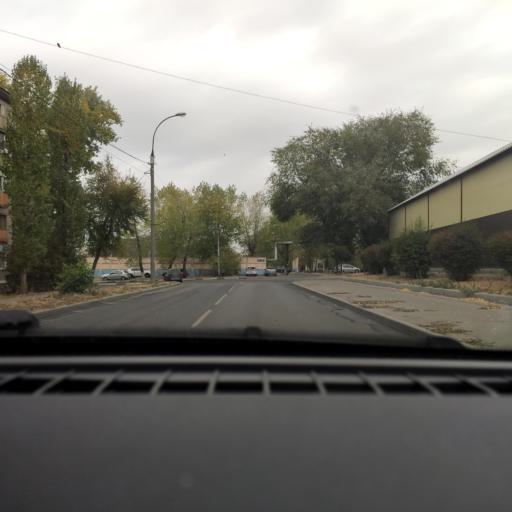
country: RU
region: Voronezj
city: Voronezh
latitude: 51.6411
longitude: 39.2460
